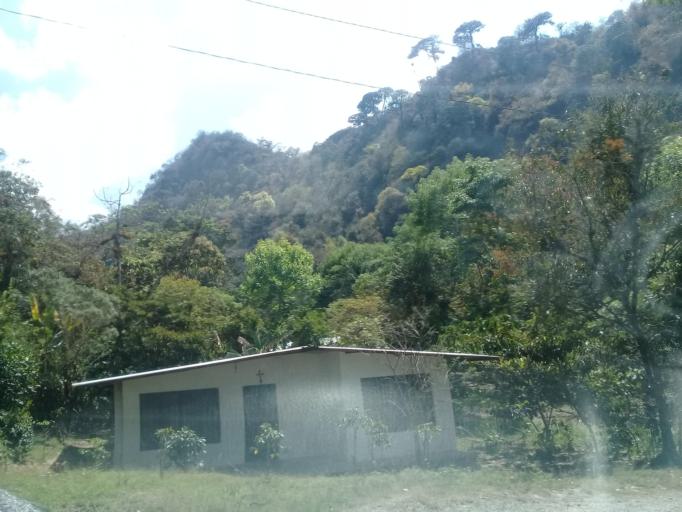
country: MX
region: Veracruz
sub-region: Tlilapan
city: Tonalixco
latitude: 18.8085
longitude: -97.0642
